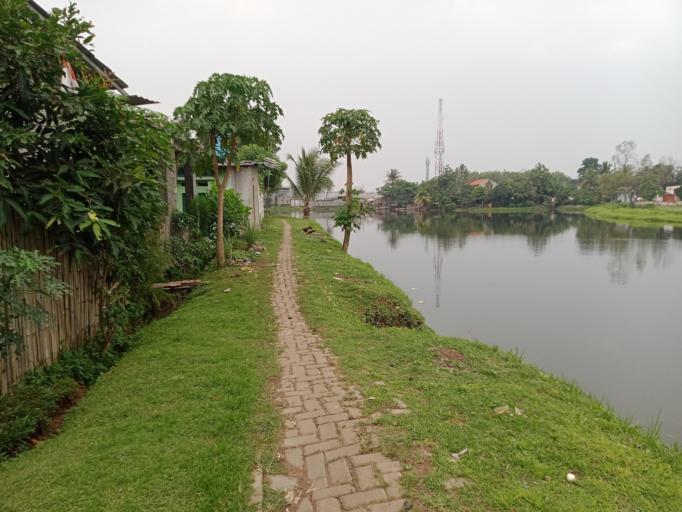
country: ID
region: West Java
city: Pasarkemis
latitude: -6.1994
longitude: 106.5233
